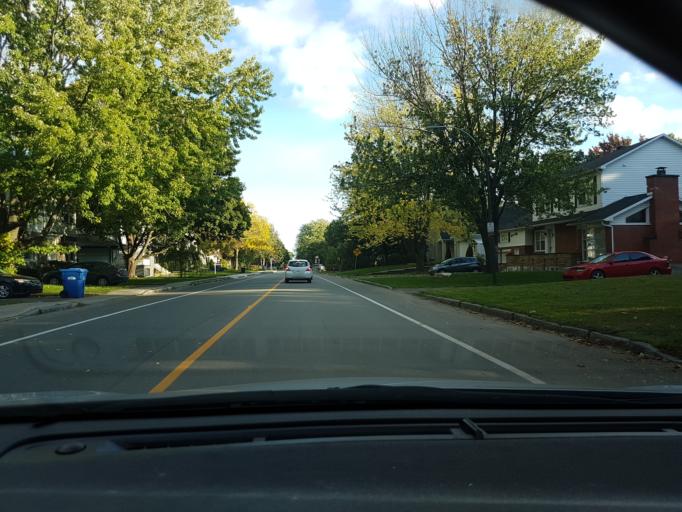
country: CA
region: Quebec
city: Quebec
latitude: 46.7739
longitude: -71.2722
